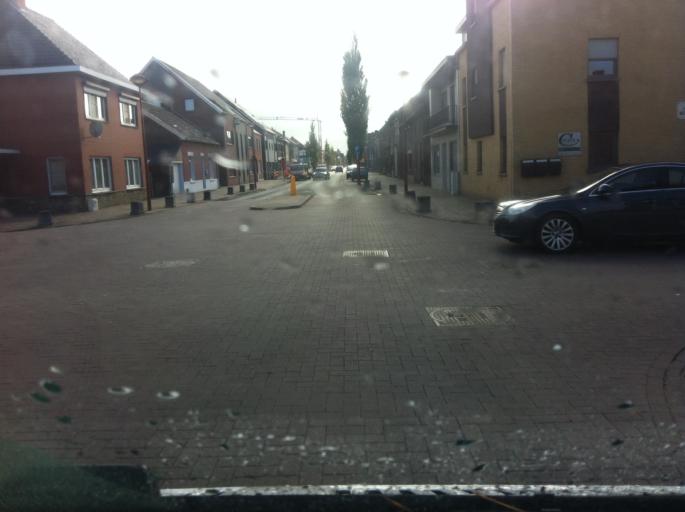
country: BE
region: Flanders
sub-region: Provincie Limburg
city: Maasmechelen
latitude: 50.9683
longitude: 5.6866
